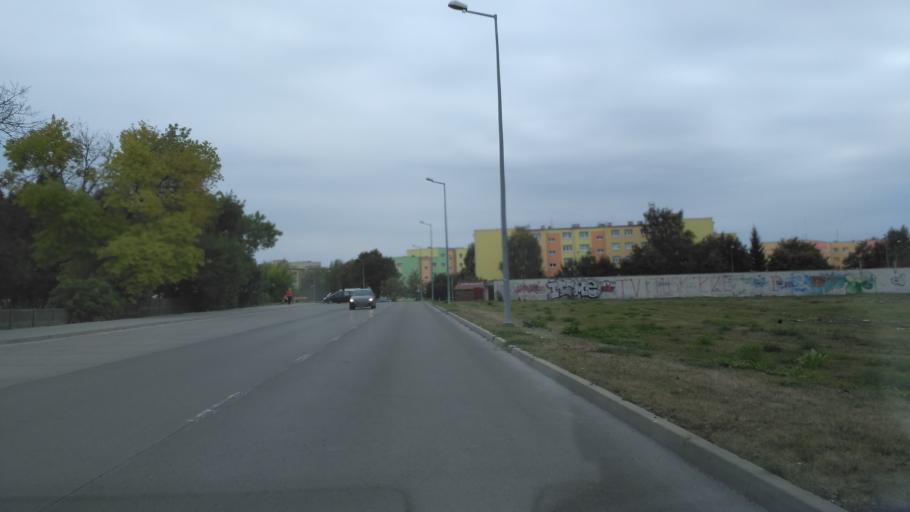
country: PL
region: Lublin Voivodeship
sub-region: Chelm
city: Chelm
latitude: 51.1280
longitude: 23.4660
